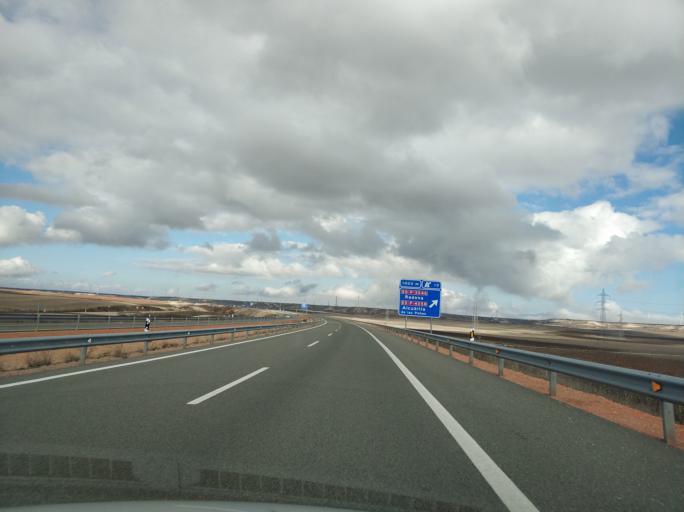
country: ES
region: Castille and Leon
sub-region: Provincia de Soria
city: Yelo
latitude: 41.2461
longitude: -2.4757
